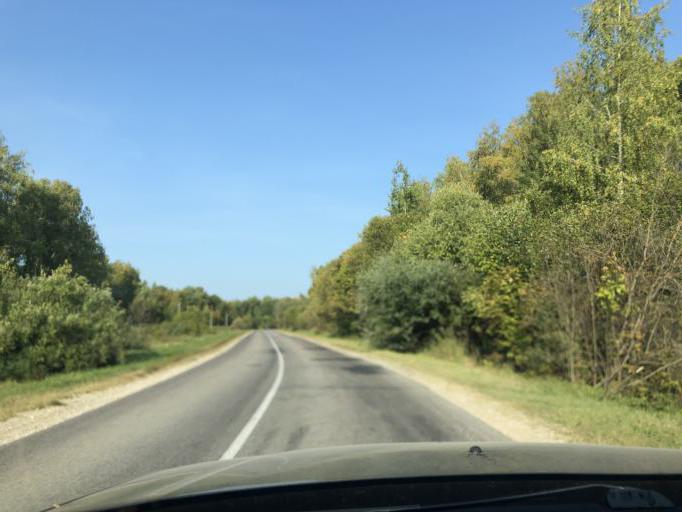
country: RU
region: Tula
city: Leninskiy
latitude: 54.3314
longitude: 37.3901
